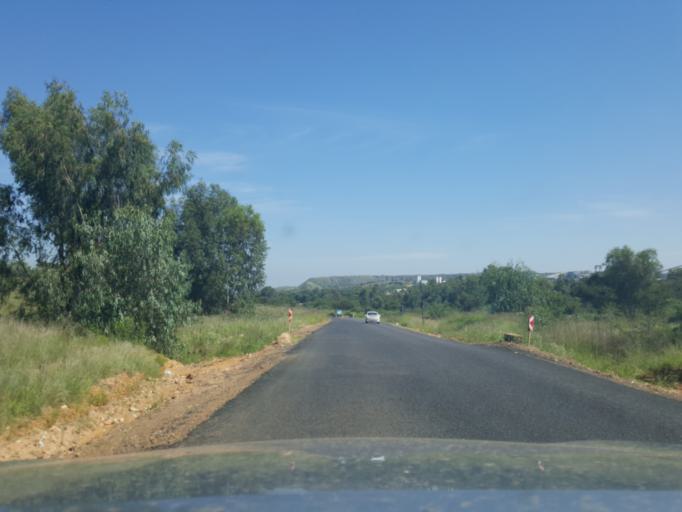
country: ZA
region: Gauteng
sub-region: City of Tshwane Metropolitan Municipality
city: Cullinan
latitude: -25.6860
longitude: 28.5165
